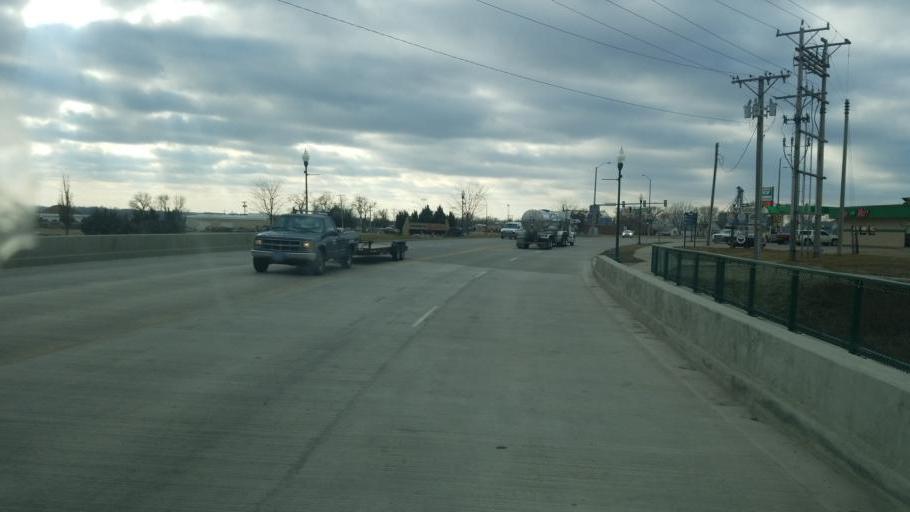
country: US
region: South Dakota
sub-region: Yankton County
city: Yankton
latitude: 42.8718
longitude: -97.3813
